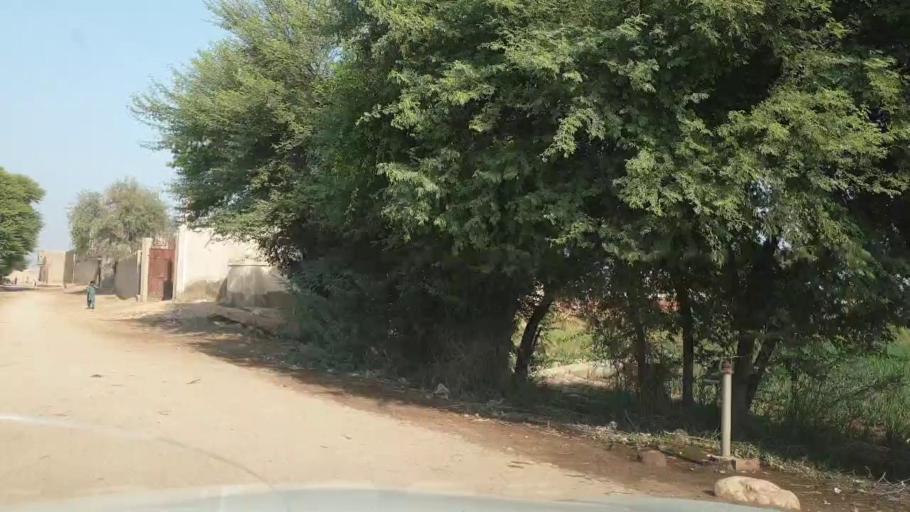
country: PK
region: Sindh
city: Bhan
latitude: 26.5456
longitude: 67.7435
